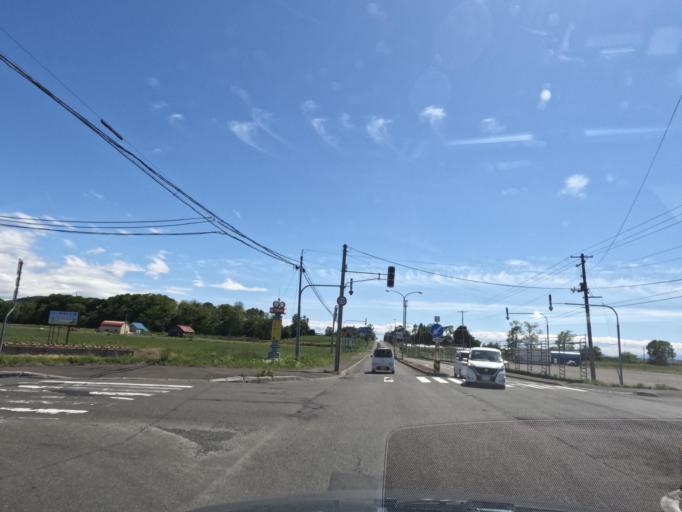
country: JP
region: Hokkaido
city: Iwamizawa
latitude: 43.0640
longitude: 141.7372
